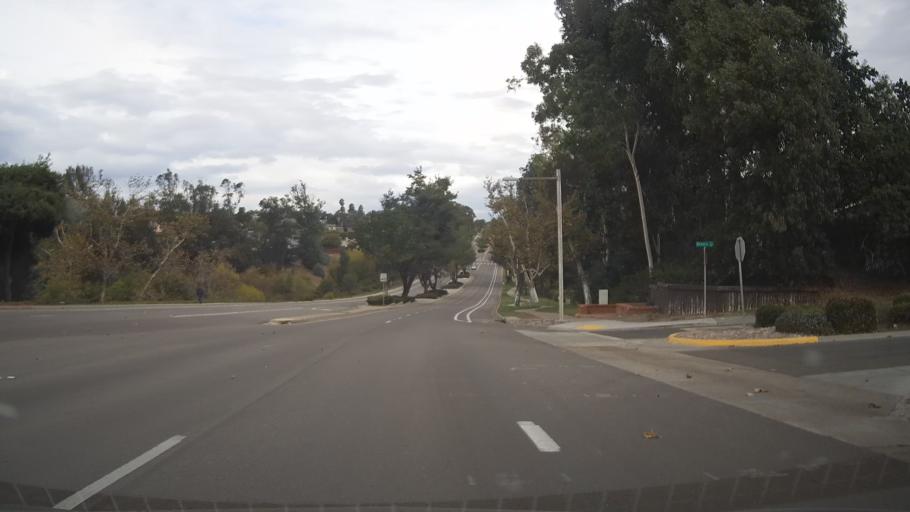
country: US
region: California
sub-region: San Diego County
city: La Mesa
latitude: 32.8307
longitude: -117.1028
